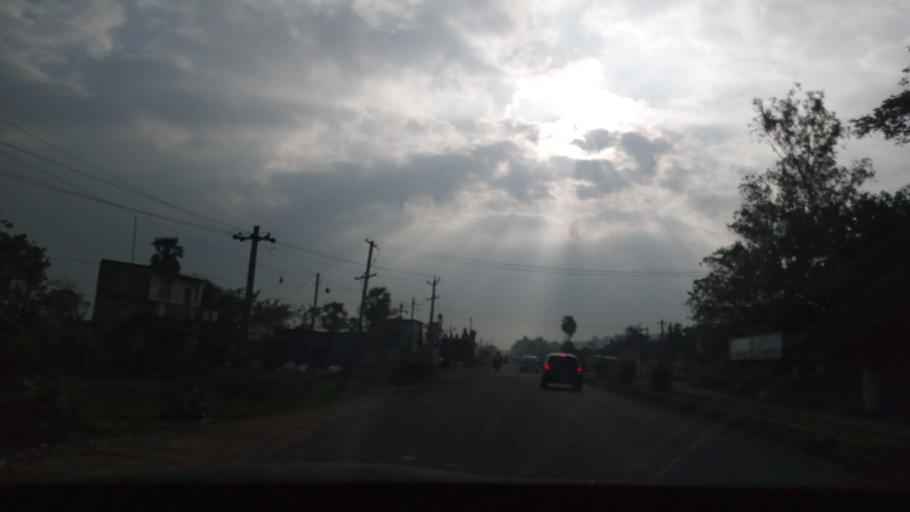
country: IN
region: Tamil Nadu
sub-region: Kancheepuram
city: Vandalur
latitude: 12.8671
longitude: 80.1157
